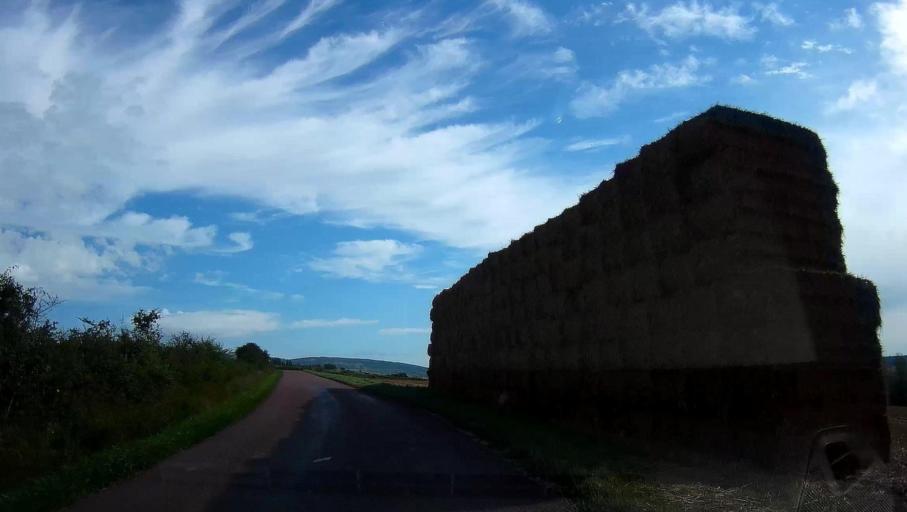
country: FR
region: Bourgogne
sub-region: Departement de Saone-et-Loire
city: Saint-Leger-sur-Dheune
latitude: 46.8796
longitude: 4.6386
